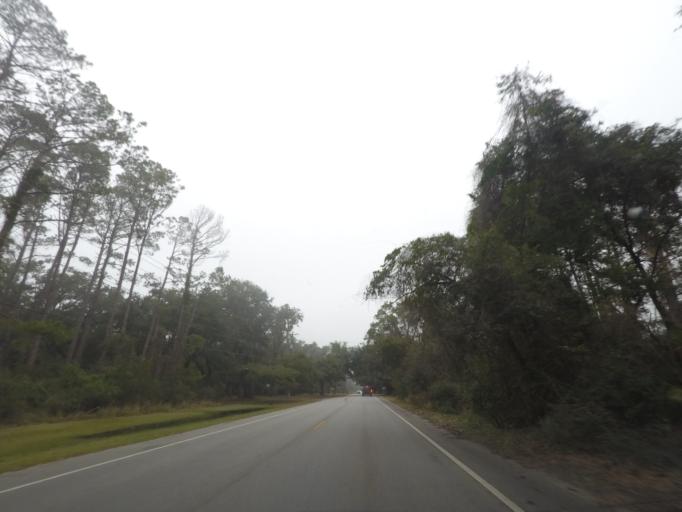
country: US
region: South Carolina
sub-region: Charleston County
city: Seabrook Island
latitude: 32.5118
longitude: -80.2997
